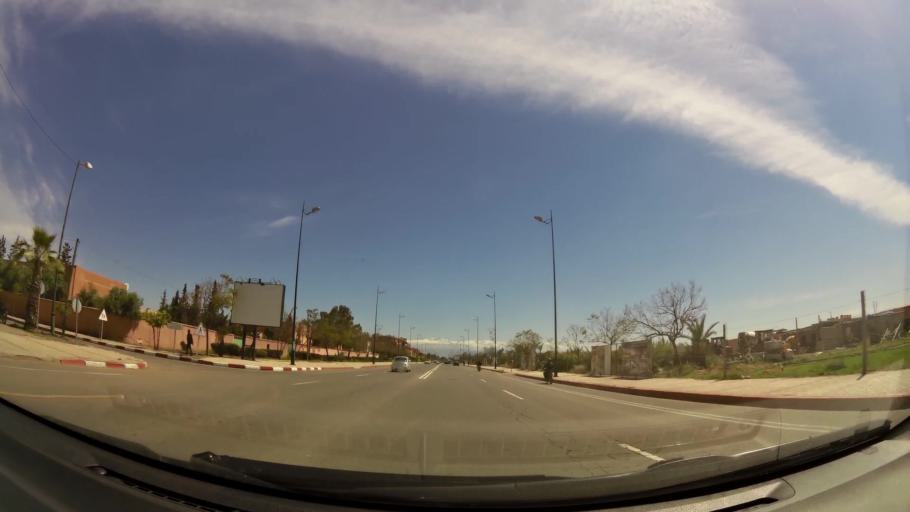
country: MA
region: Marrakech-Tensift-Al Haouz
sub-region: Marrakech
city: Marrakesh
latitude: 31.6098
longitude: -7.9737
